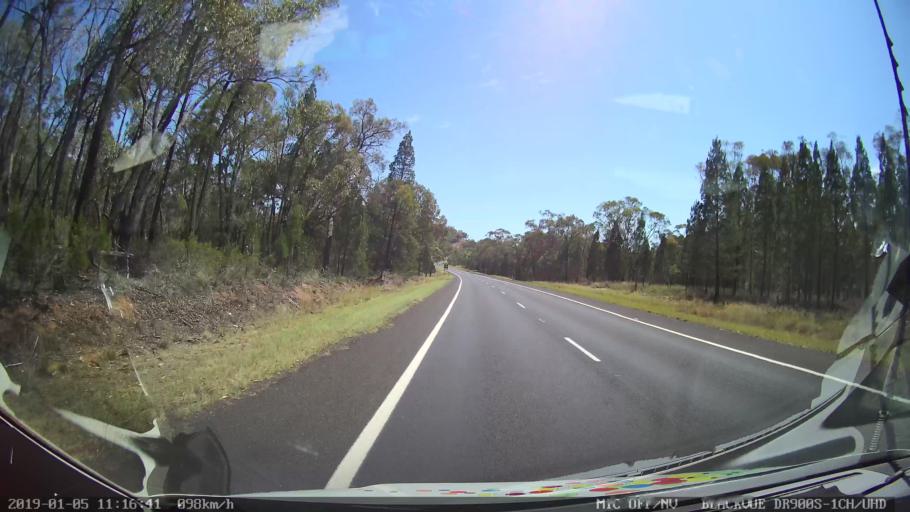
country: AU
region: New South Wales
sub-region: Warrumbungle Shire
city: Coonabarabran
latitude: -31.3355
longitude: 149.3002
